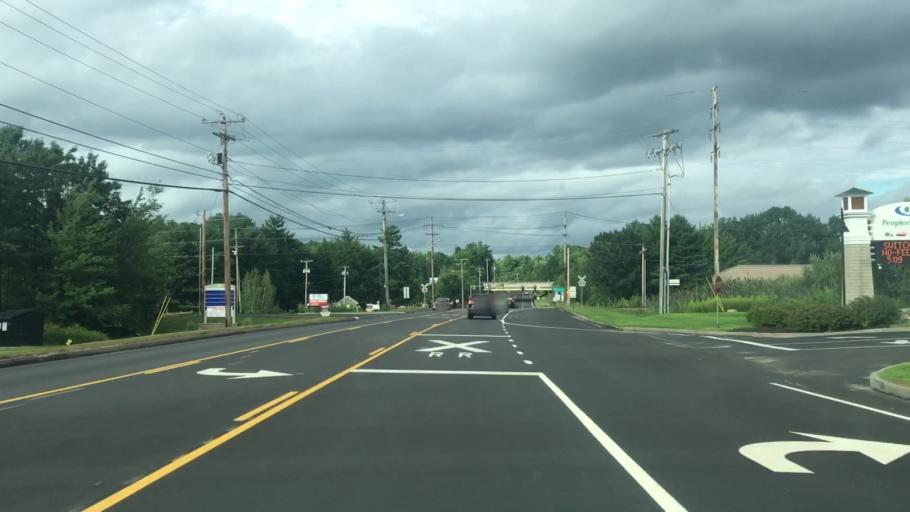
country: US
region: Maine
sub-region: York County
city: Saco
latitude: 43.5206
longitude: -70.4487
